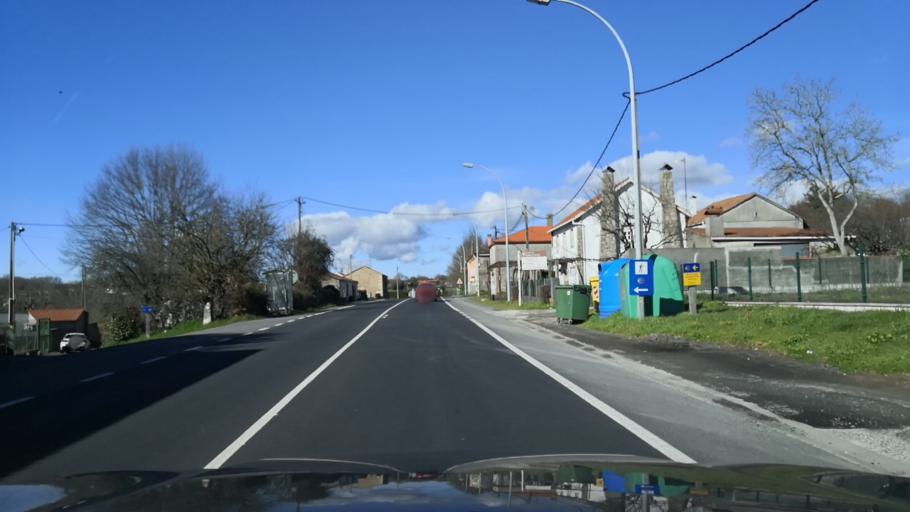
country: ES
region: Galicia
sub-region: Provincia de Pontevedra
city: Lalin
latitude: 42.6787
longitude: -8.1659
